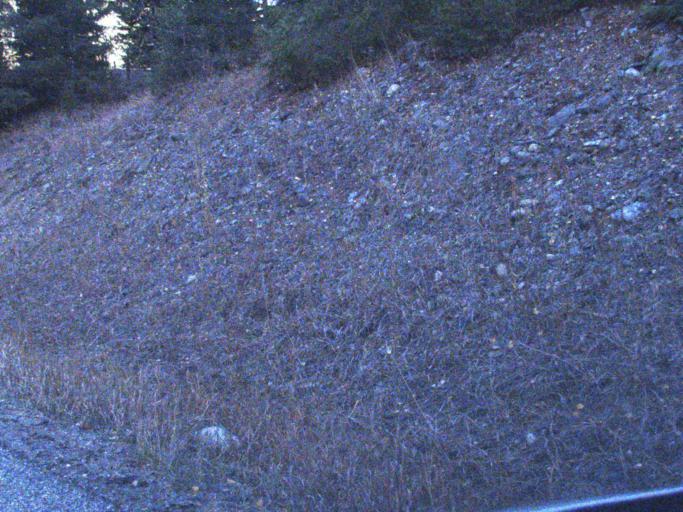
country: CA
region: British Columbia
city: Rossland
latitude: 48.9837
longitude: -117.8265
